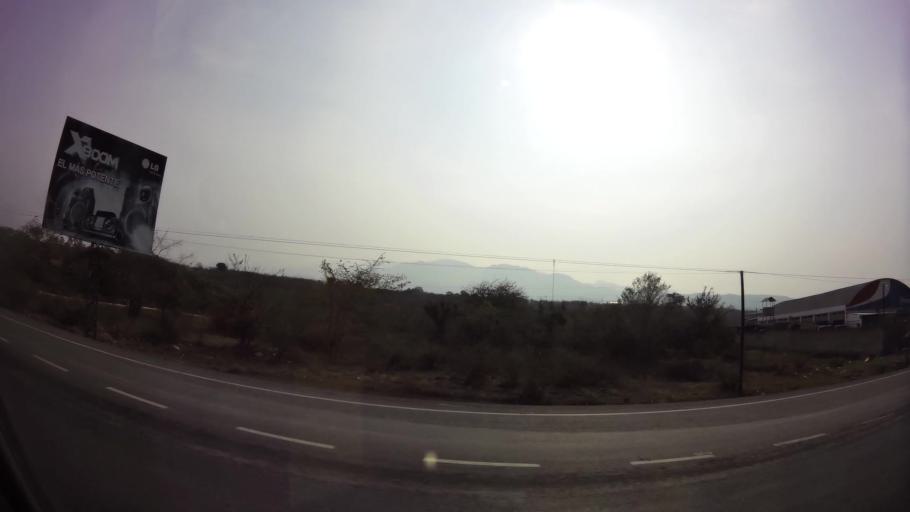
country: HN
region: Comayagua
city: Comayagua
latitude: 14.4165
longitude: -87.6250
